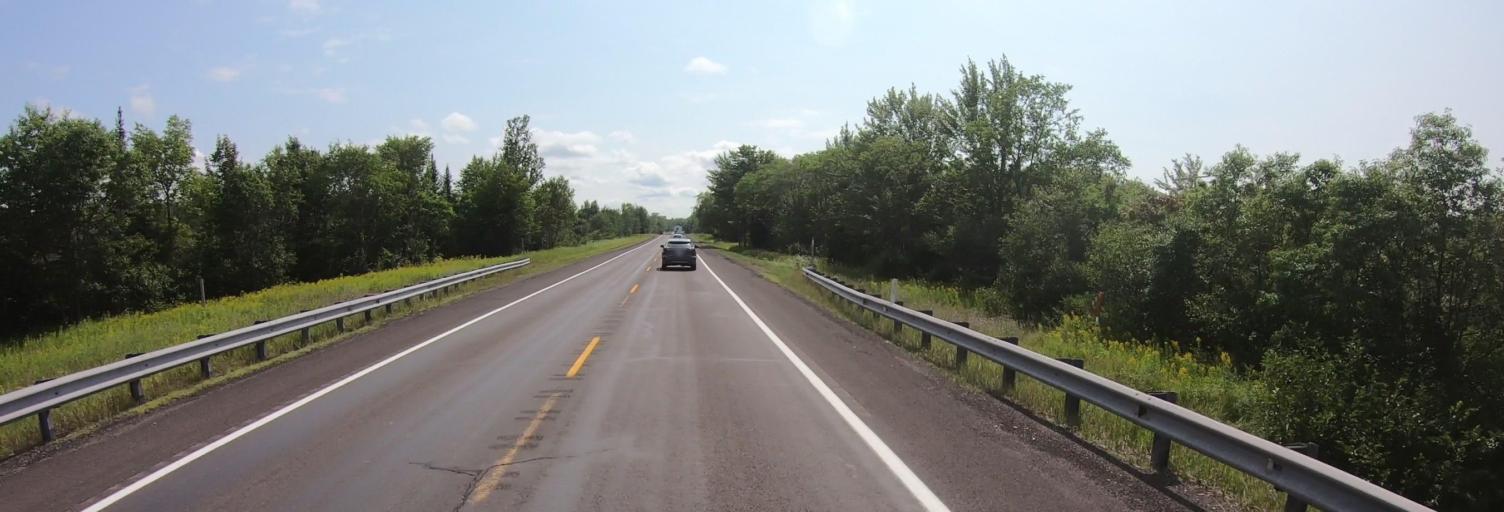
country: US
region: Michigan
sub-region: Houghton County
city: Hancock
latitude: 46.8821
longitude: -88.8659
